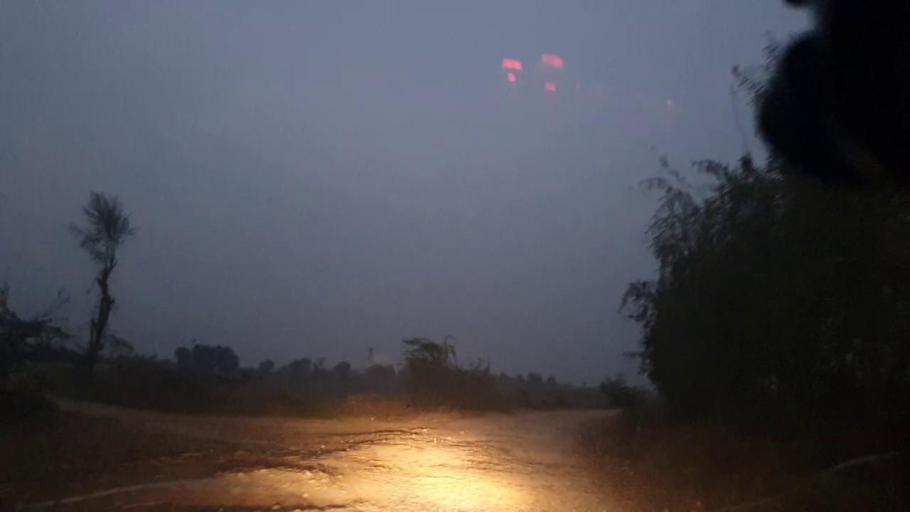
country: PK
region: Sindh
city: Hingorja
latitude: 27.2096
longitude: 68.3715
